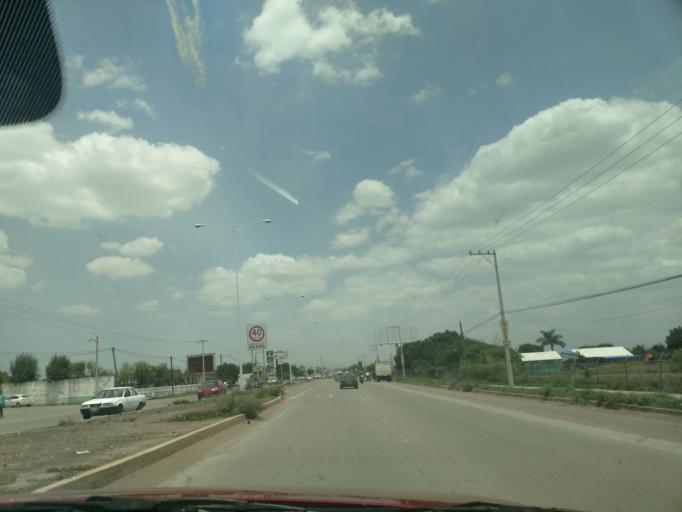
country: MX
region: San Luis Potosi
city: Ciudad Fernandez
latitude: 21.9362
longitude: -100.0281
